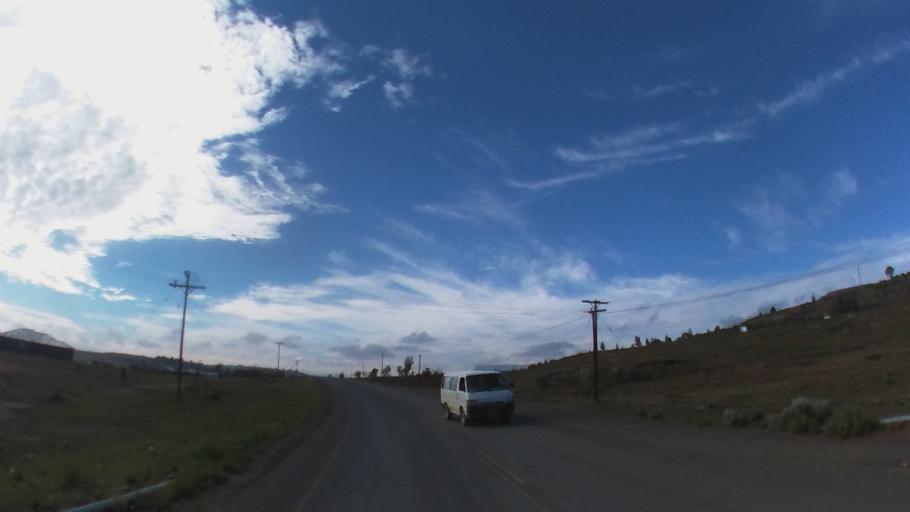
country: LS
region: Maseru
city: Maseru
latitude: -29.3886
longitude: 27.4706
